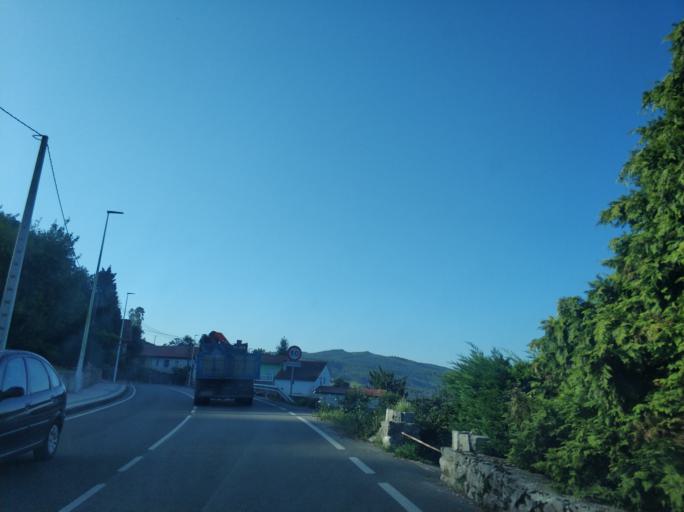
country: ES
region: Cantabria
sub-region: Provincia de Cantabria
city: Polanco
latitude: 43.3642
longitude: -3.9576
